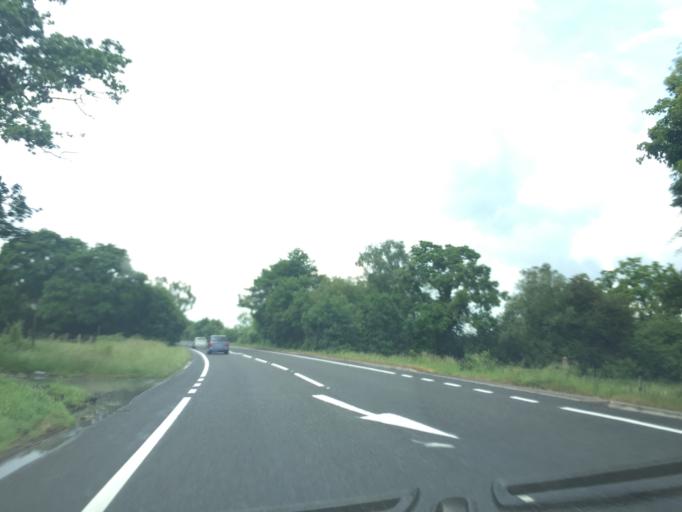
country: GB
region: England
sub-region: Dorset
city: Wareham
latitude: 50.6753
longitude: -2.1135
